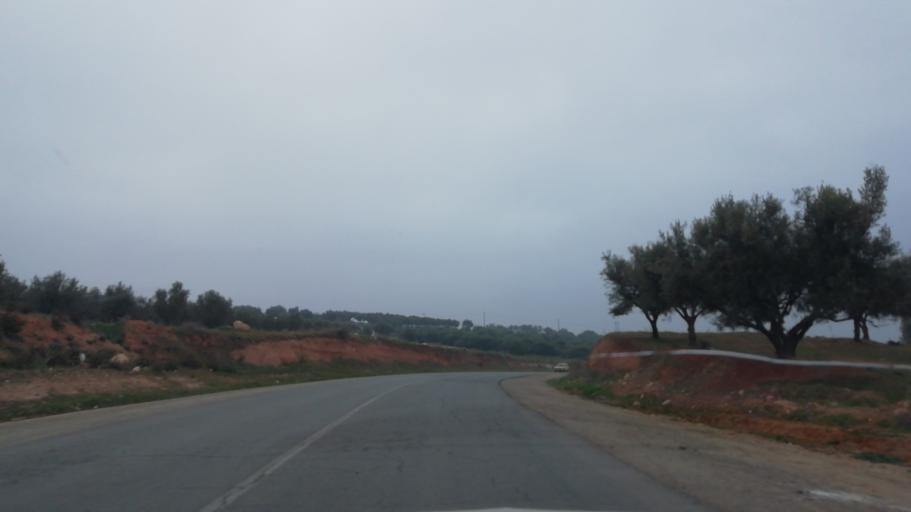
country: DZ
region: Mascara
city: Mascara
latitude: 35.3877
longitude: 0.1621
